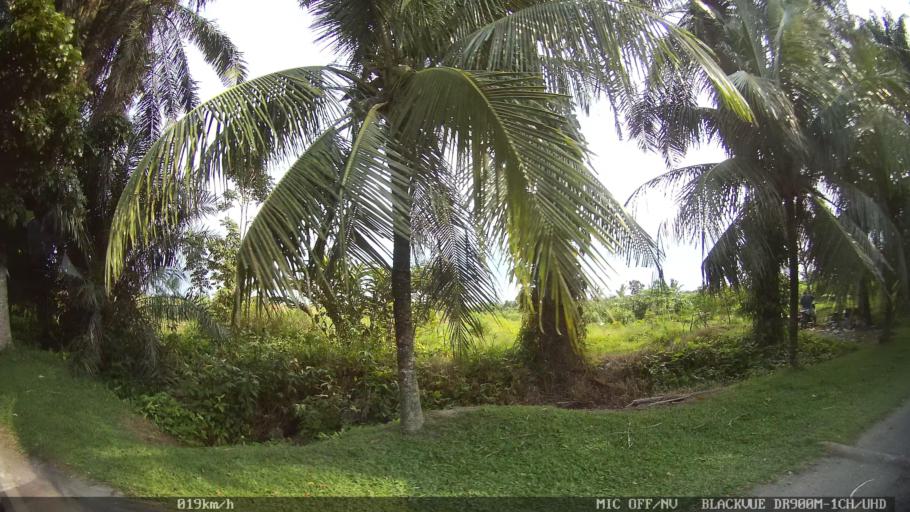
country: ID
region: North Sumatra
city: Binjai
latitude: 3.6030
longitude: 98.5077
